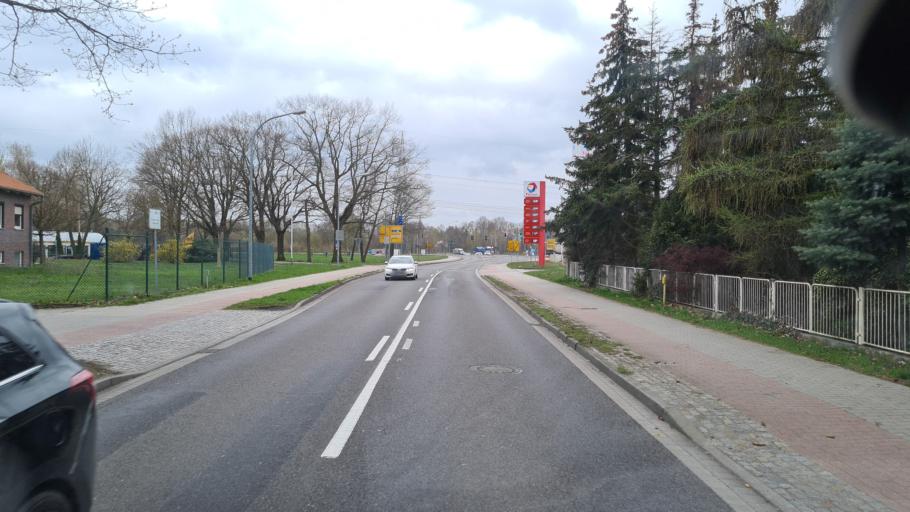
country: DE
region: Brandenburg
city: Ruhland
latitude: 51.4672
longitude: 13.8686
